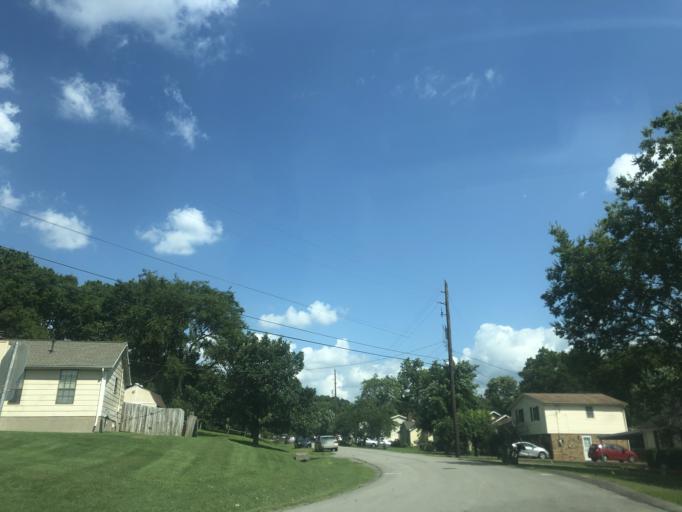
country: US
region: Tennessee
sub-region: Wilson County
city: Green Hill
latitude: 36.2050
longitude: -86.5866
